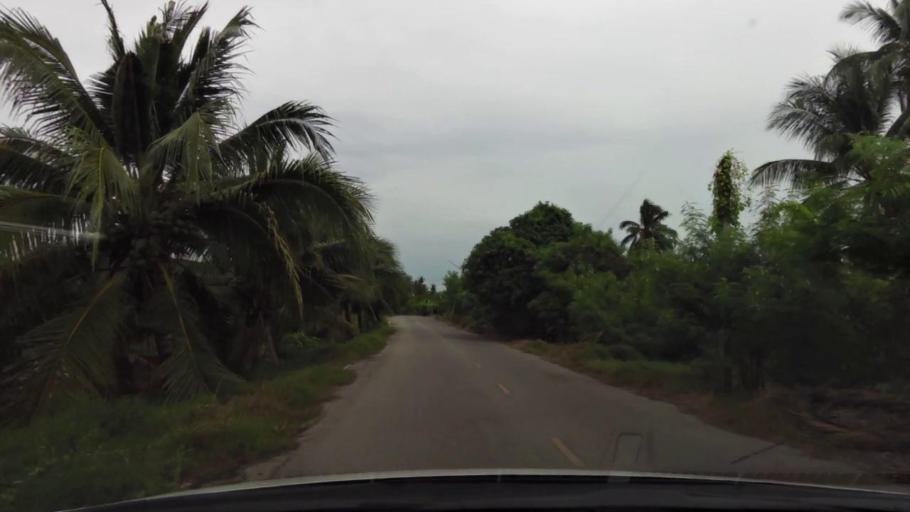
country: TH
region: Ratchaburi
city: Damnoen Saduak
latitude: 13.5669
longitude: 100.0214
